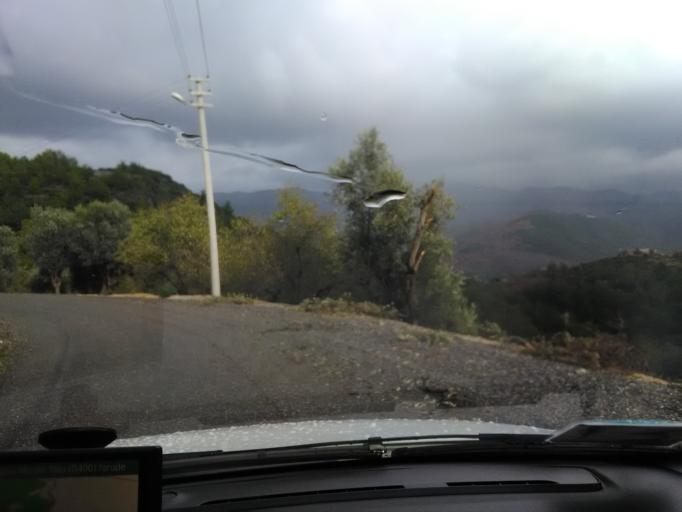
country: TR
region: Antalya
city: Gazipasa
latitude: 36.1629
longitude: 32.4335
